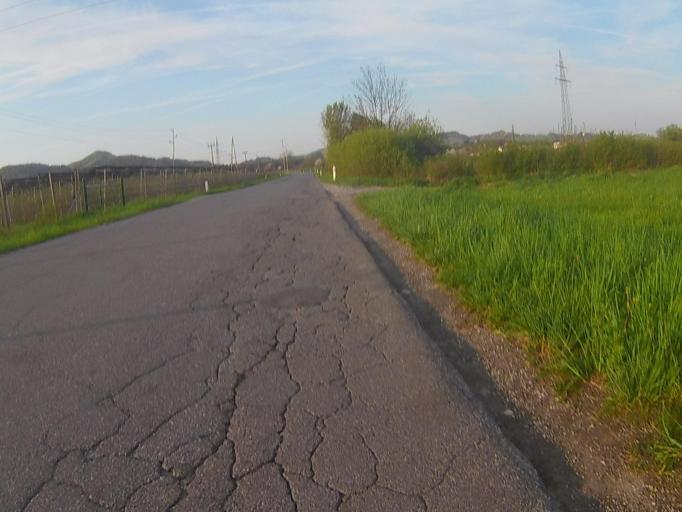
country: SI
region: Maribor
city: Pekre
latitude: 46.5536
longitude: 15.5989
